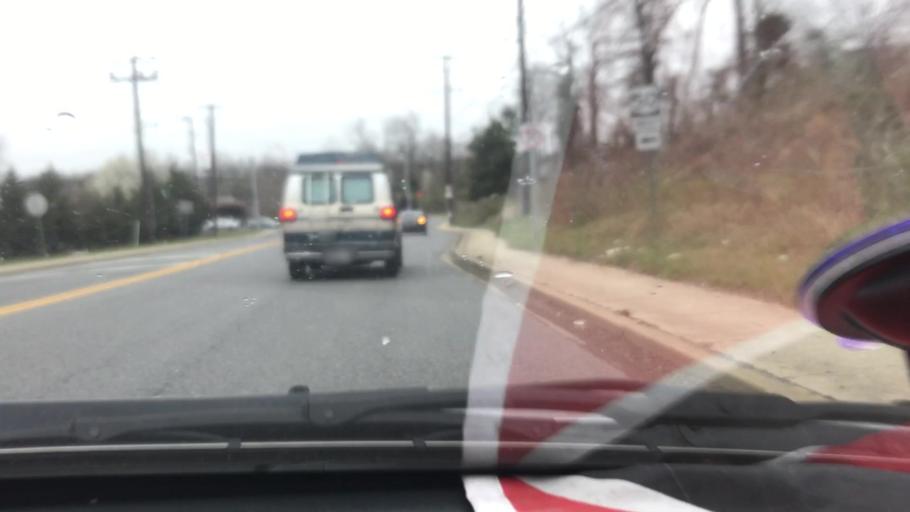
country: US
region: Maryland
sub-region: Prince George's County
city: Cheverly
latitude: 38.9160
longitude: -76.9057
